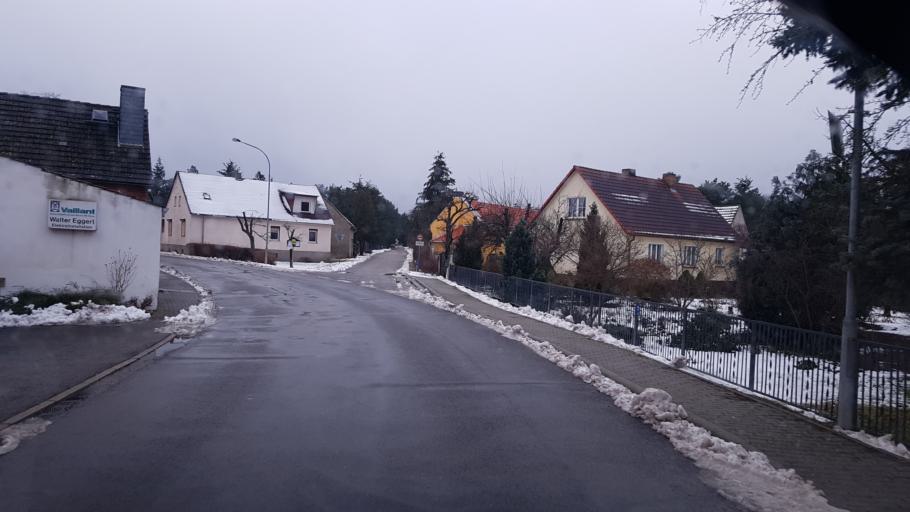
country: DE
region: Brandenburg
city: Schenkendobern
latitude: 51.9324
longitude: 14.6206
